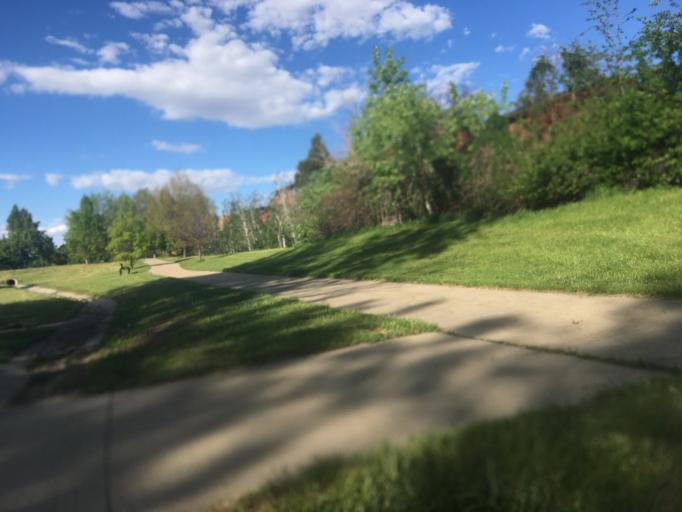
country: US
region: Colorado
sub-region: Boulder County
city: Louisville
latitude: 39.9880
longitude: -105.1606
